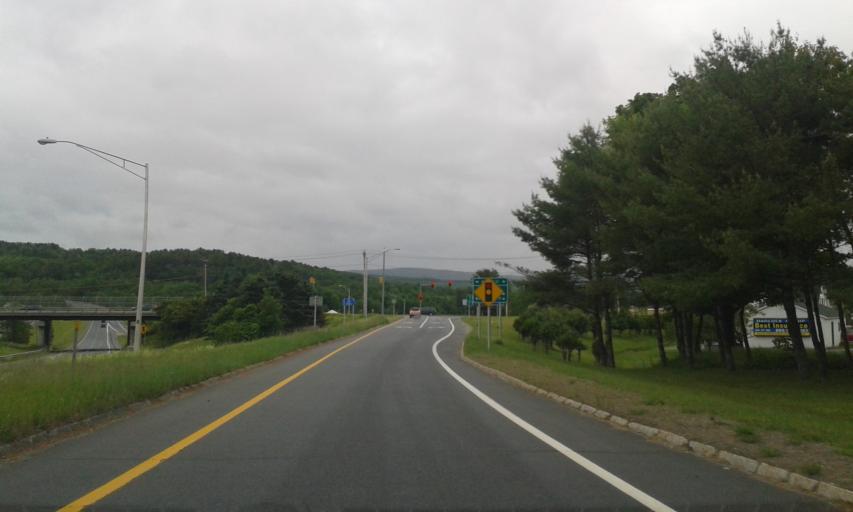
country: US
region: New Hampshire
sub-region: Grafton County
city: Littleton
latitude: 44.3095
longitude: -71.8000
